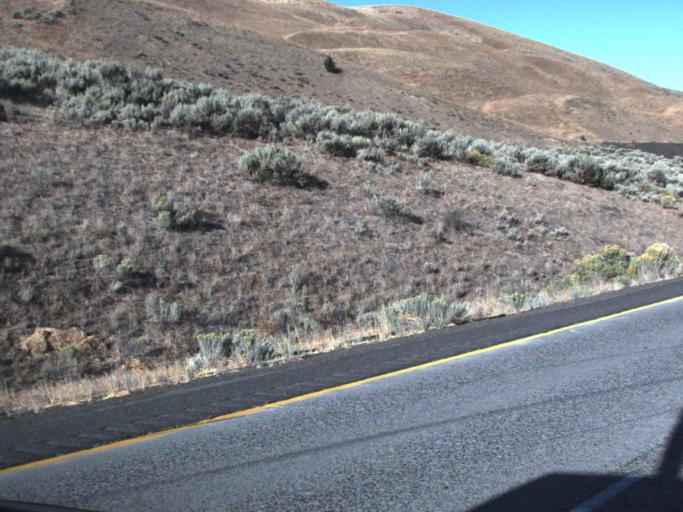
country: US
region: Washington
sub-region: Kittitas County
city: Kittitas
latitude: 46.8927
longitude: -120.4396
